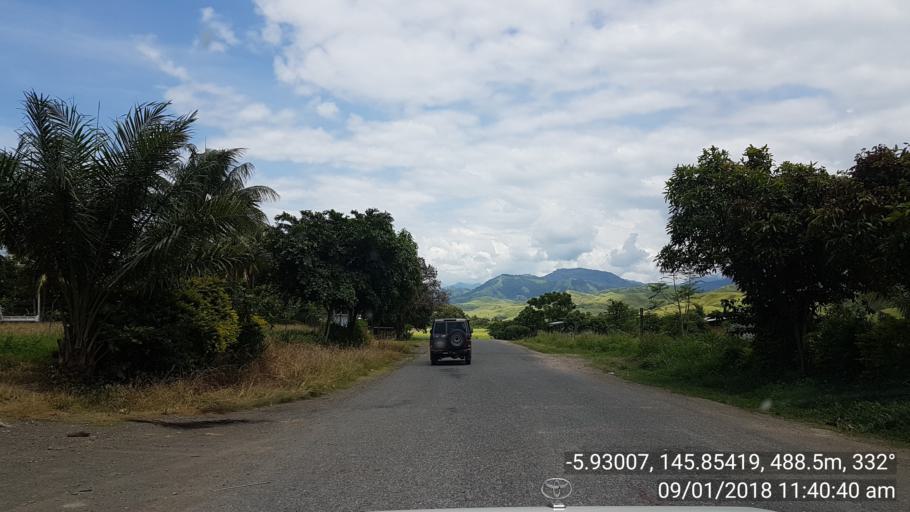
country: PG
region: Eastern Highlands
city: Kainantu
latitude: -5.9304
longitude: 145.8545
